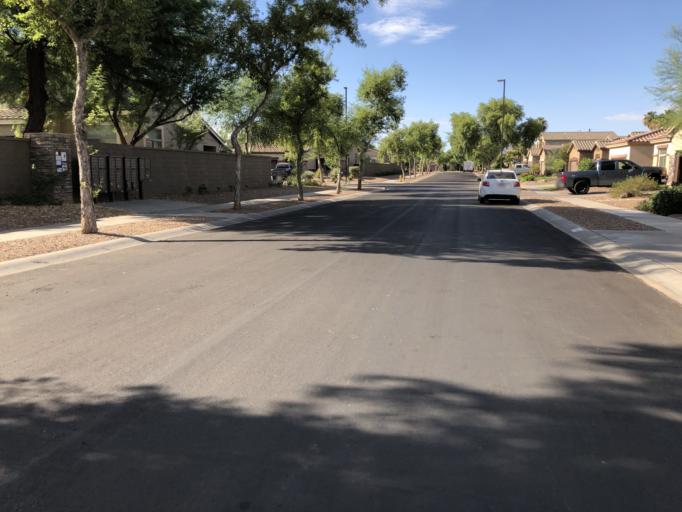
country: US
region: Arizona
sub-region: Maricopa County
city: Queen Creek
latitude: 33.2668
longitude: -111.7029
